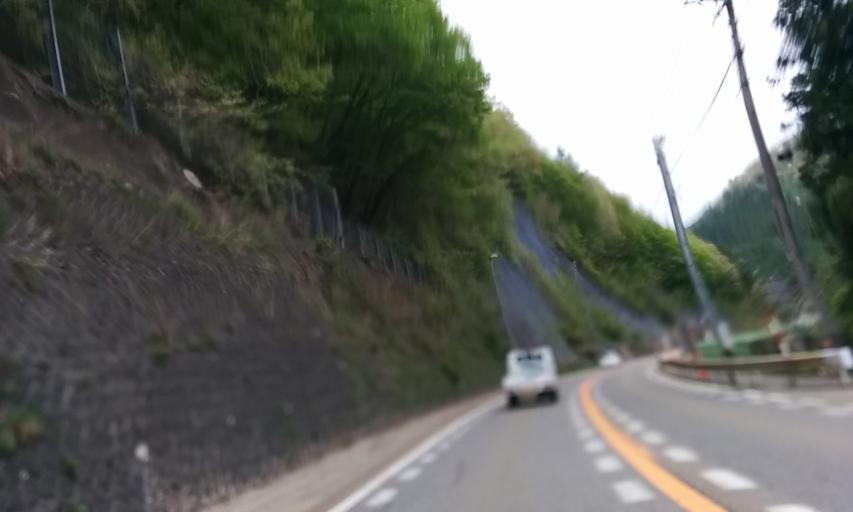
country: JP
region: Gifu
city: Takayama
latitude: 36.0990
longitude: 137.2592
